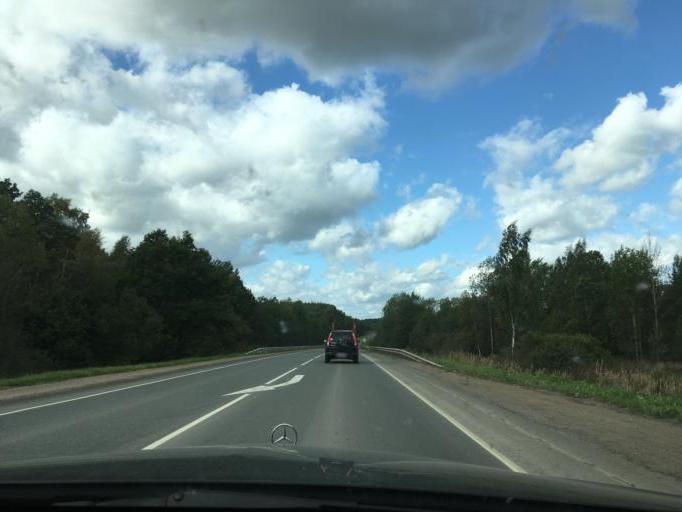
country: RU
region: Pskov
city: Novosokol'niki
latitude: 56.3010
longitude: 30.2146
